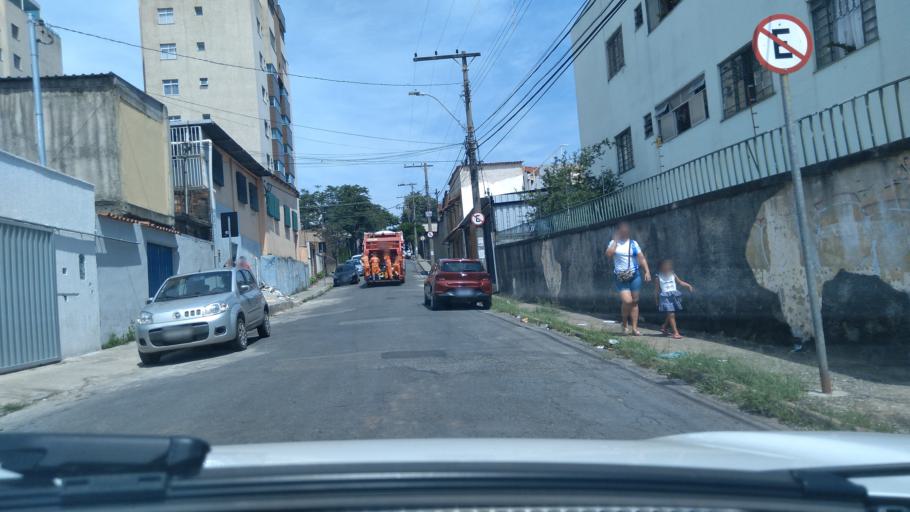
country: BR
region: Minas Gerais
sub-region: Contagem
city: Contagem
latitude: -19.9273
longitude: -44.0036
